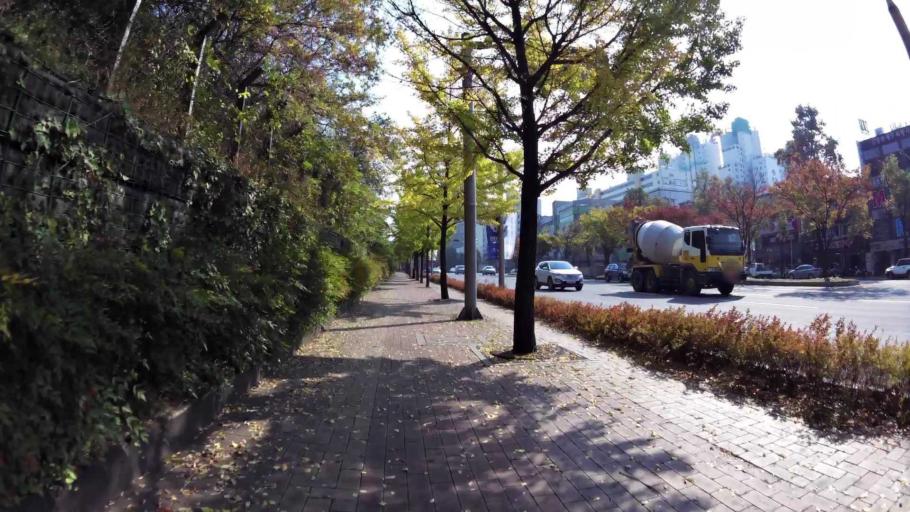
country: KR
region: Daegu
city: Daegu
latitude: 35.8559
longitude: 128.6525
